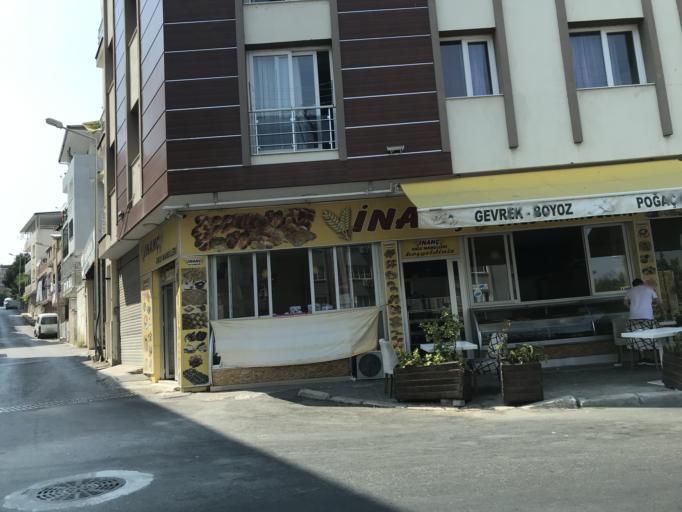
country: TR
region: Izmir
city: Karabaglar
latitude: 38.3838
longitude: 27.1138
